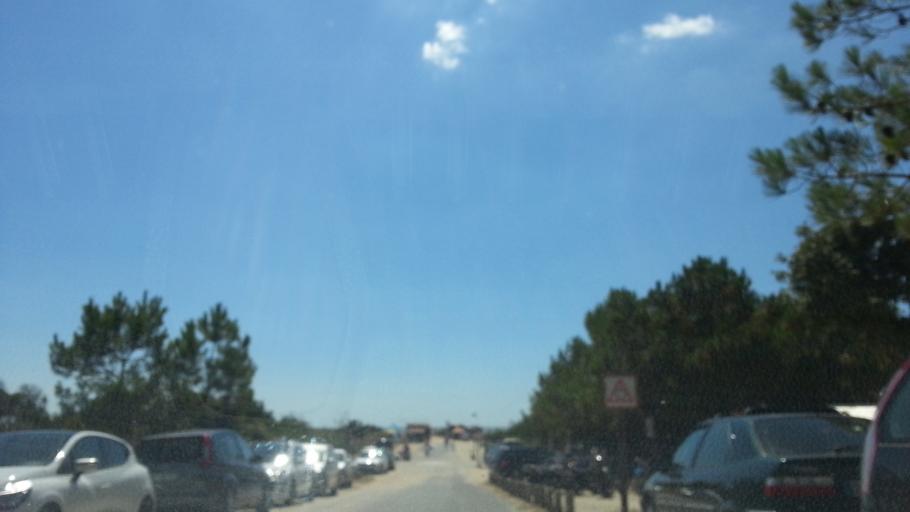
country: FR
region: Poitou-Charentes
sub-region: Departement de la Charente-Maritime
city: Dolus-d'Oleron
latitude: 45.8775
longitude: -1.2614
